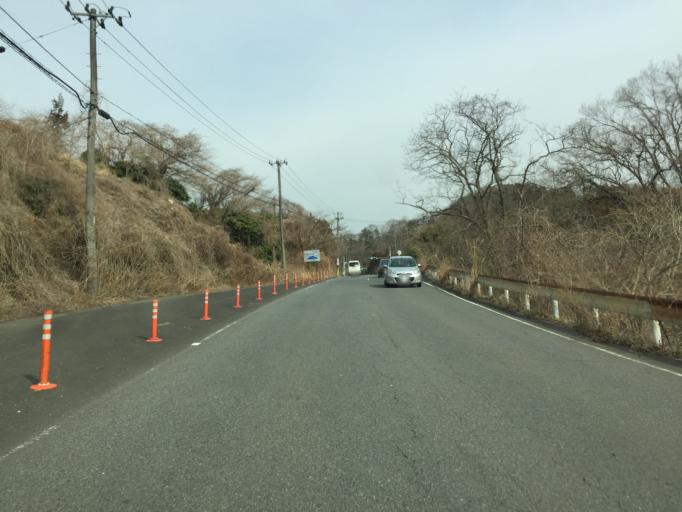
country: JP
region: Fukushima
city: Iwaki
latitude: 37.0035
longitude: 140.8170
